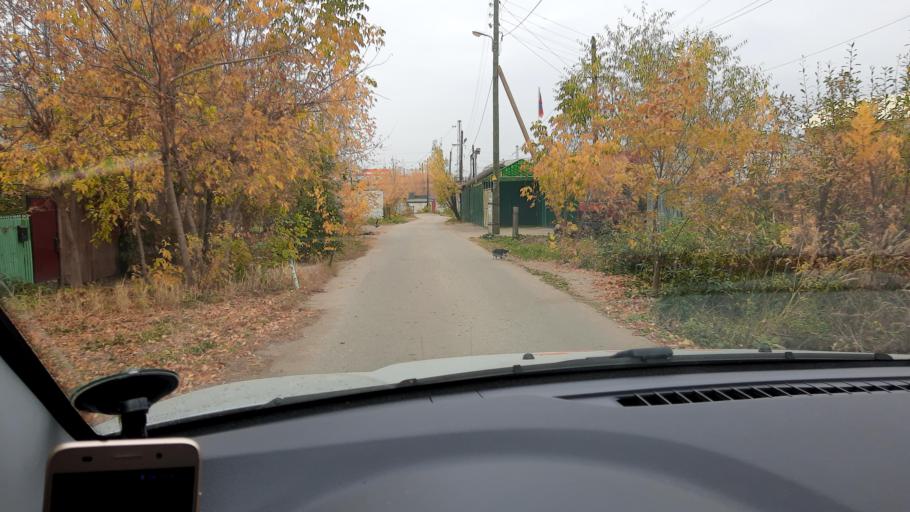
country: RU
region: Nizjnij Novgorod
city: Nizhniy Novgorod
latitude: 56.3129
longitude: 43.9275
